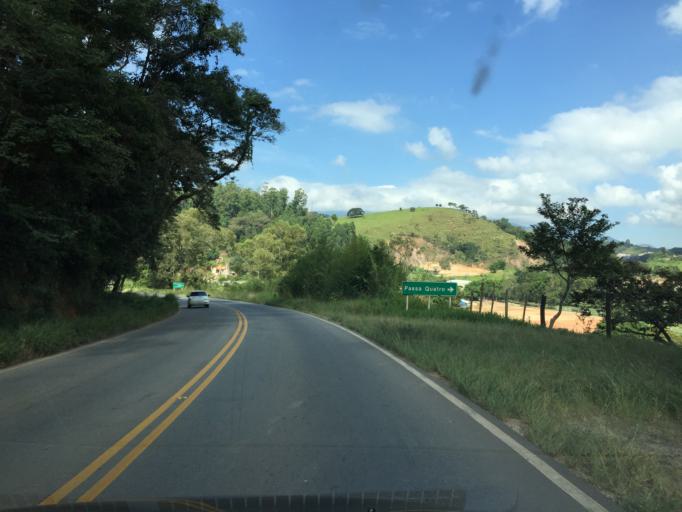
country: BR
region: Minas Gerais
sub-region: Passa Quatro
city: Passa Quatro
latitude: -22.3715
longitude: -44.9628
